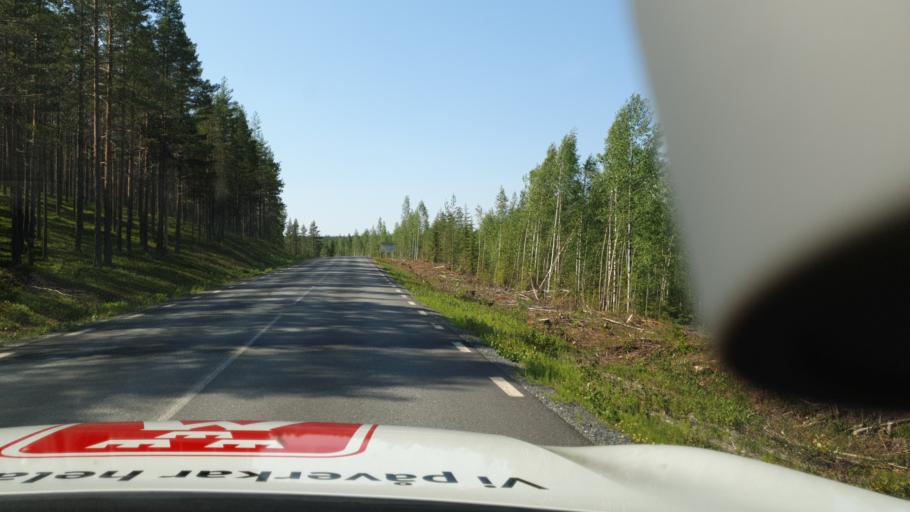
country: SE
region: Vaesterbotten
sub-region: Skelleftea Kommun
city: Langsele
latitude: 64.9511
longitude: 20.0274
